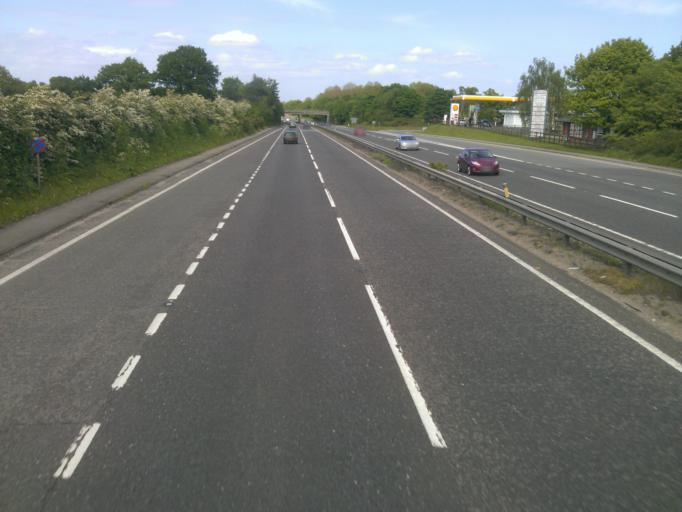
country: GB
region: England
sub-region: Suffolk
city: East Bergholt
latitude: 51.9419
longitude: 0.9545
